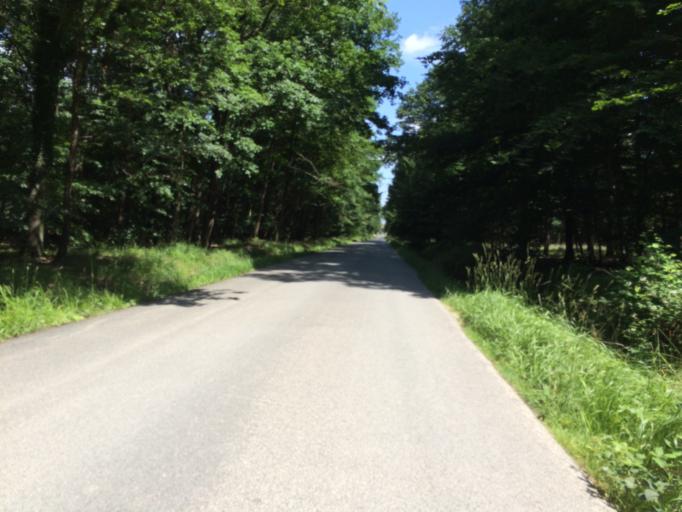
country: FR
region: Ile-de-France
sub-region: Departement de l'Essonne
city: Brunoy
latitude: 48.6799
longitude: 2.4876
